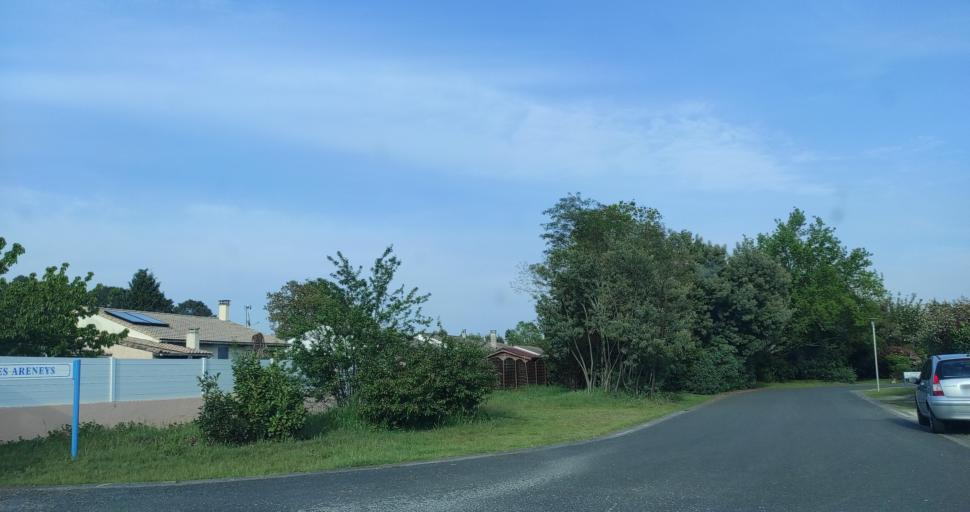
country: FR
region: Aquitaine
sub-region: Departement de la Gironde
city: Ares
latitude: 44.7636
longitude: -1.1219
